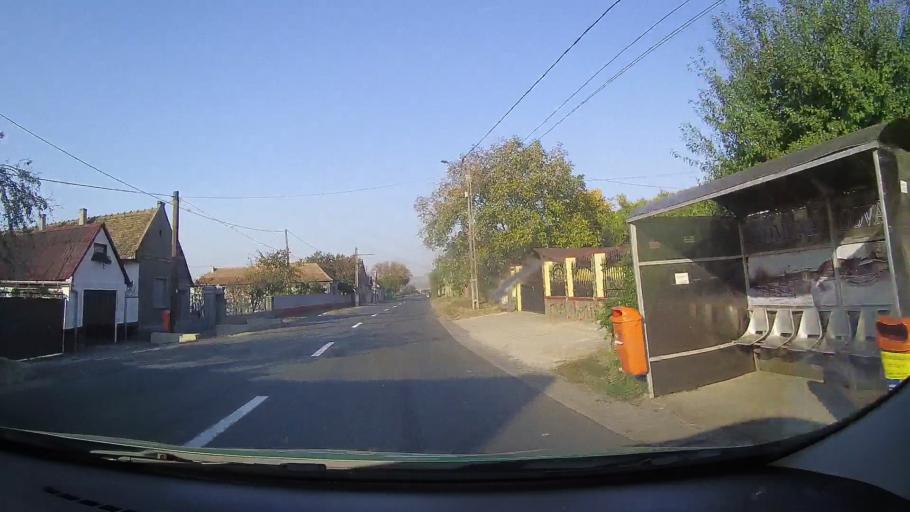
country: RO
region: Arad
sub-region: Comuna Covasint
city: Covasint
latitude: 46.2084
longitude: 21.6100
